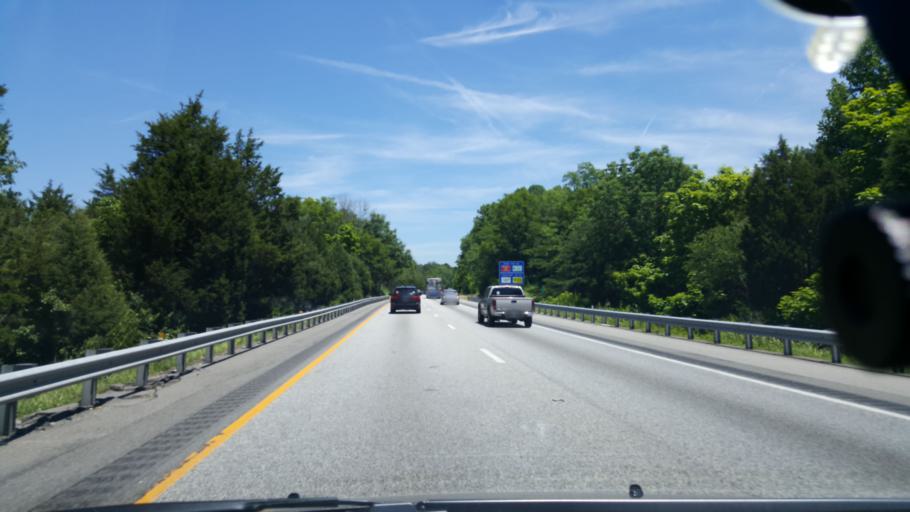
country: US
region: Virginia
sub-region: Botetourt County
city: Daleville
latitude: 37.4417
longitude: -79.8652
